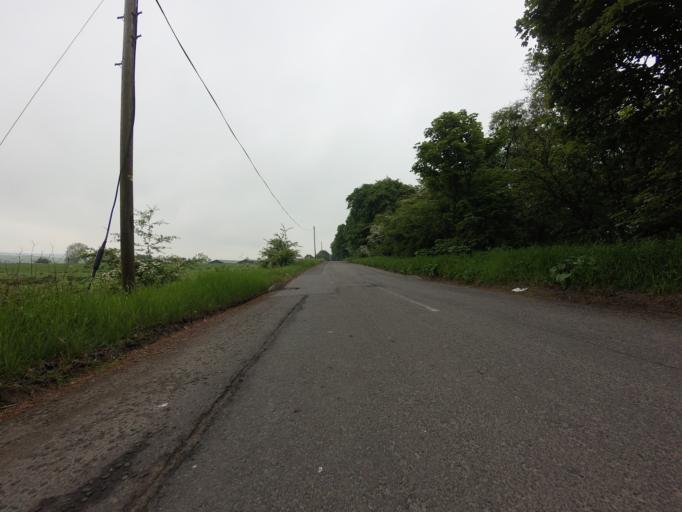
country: GB
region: Scotland
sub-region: Fife
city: Townhill
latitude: 56.0986
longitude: -3.4497
